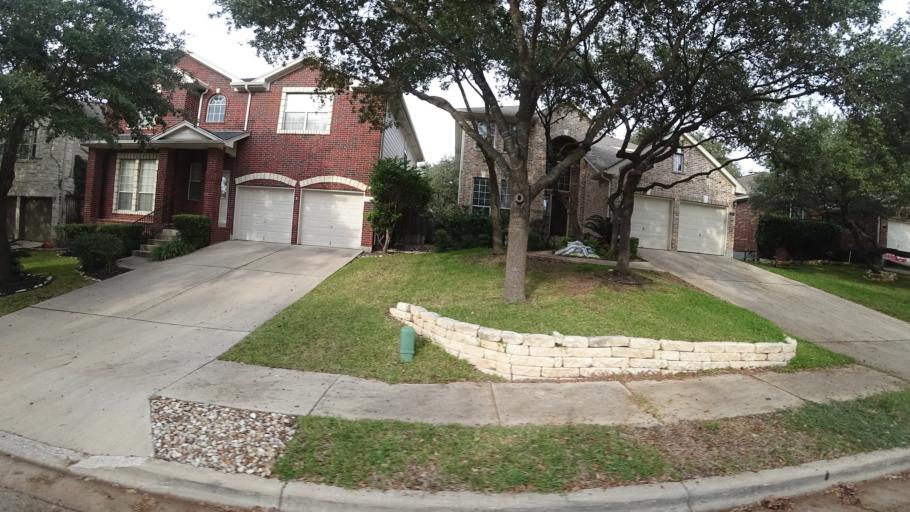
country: US
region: Texas
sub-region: Travis County
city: Hudson Bend
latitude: 30.3803
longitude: -97.8870
